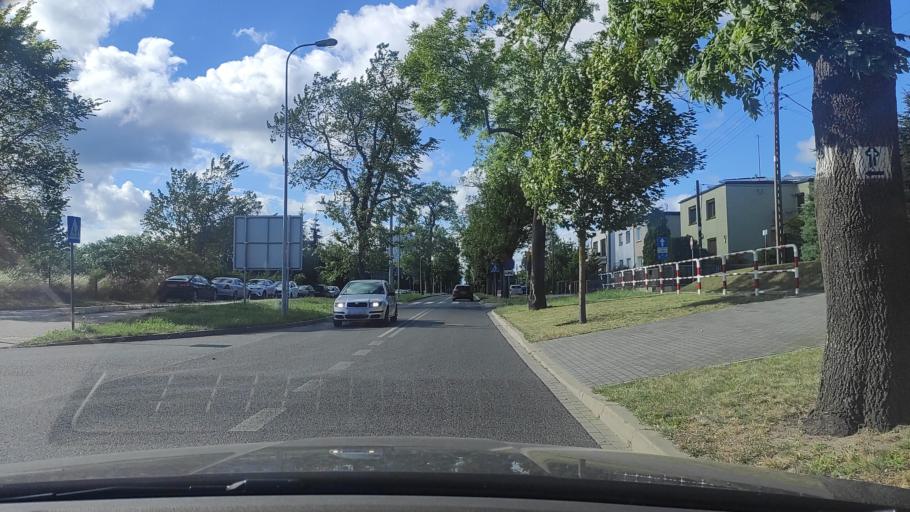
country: PL
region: Greater Poland Voivodeship
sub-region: Poznan
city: Poznan
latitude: 52.4060
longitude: 16.9835
